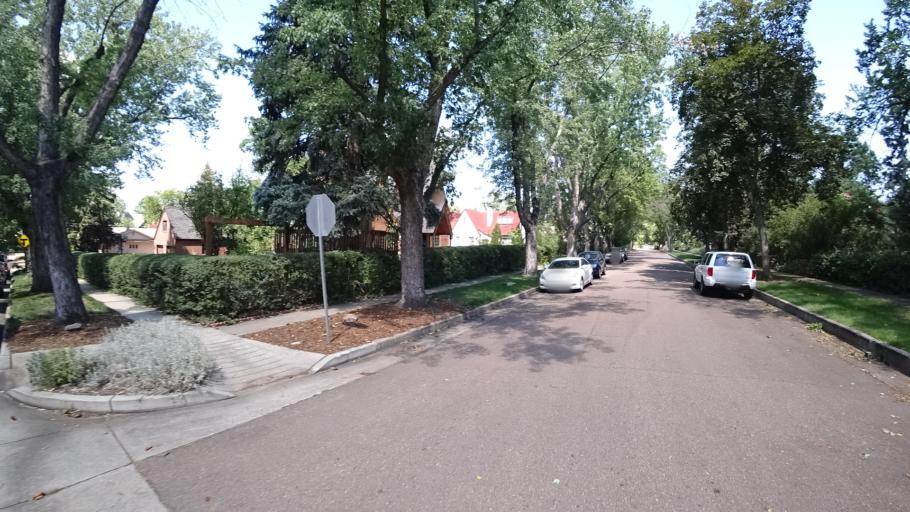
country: US
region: Colorado
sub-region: El Paso County
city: Colorado Springs
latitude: 38.8540
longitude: -104.8275
